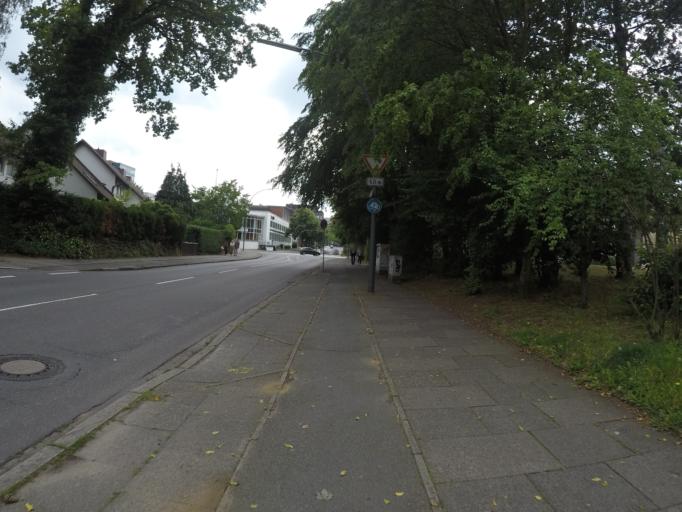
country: DE
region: Hamburg
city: Poppenbuettel
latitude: 53.6571
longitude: 10.0942
